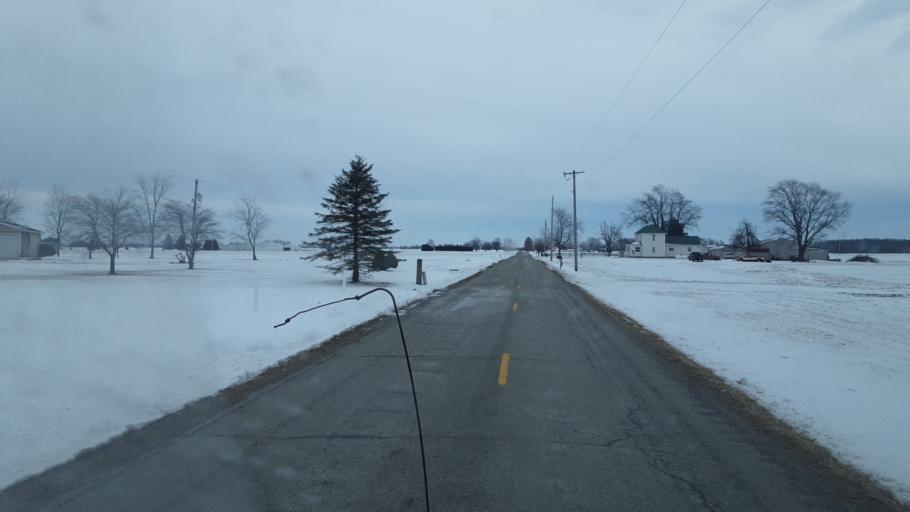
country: US
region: Ohio
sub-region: Madison County
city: Bethel
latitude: 39.7122
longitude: -83.3447
